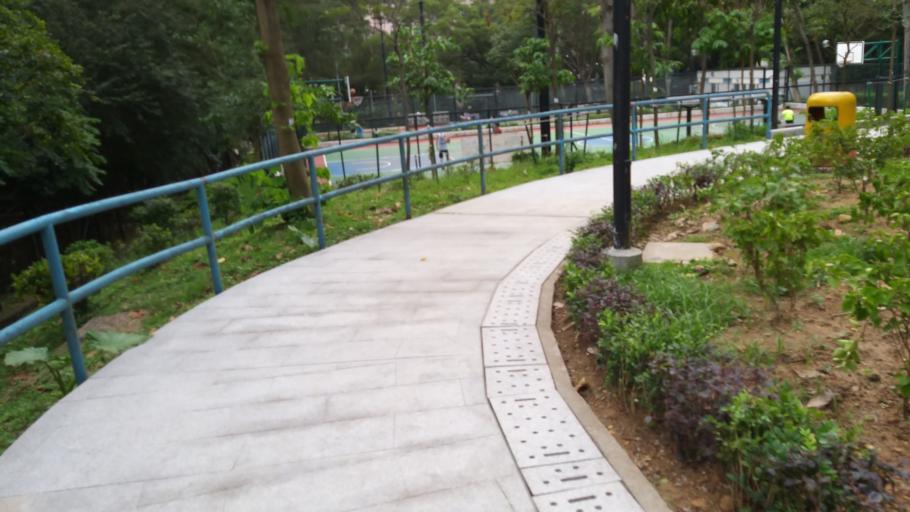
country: HK
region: Tuen Mun
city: Tuen Mun
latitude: 22.3835
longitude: 113.9824
